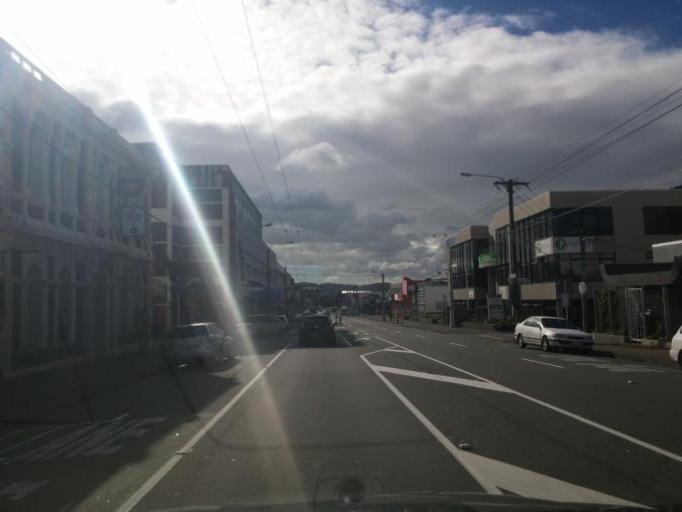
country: NZ
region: Wellington
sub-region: Wellington City
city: Wellington
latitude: -41.3055
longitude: 174.7784
